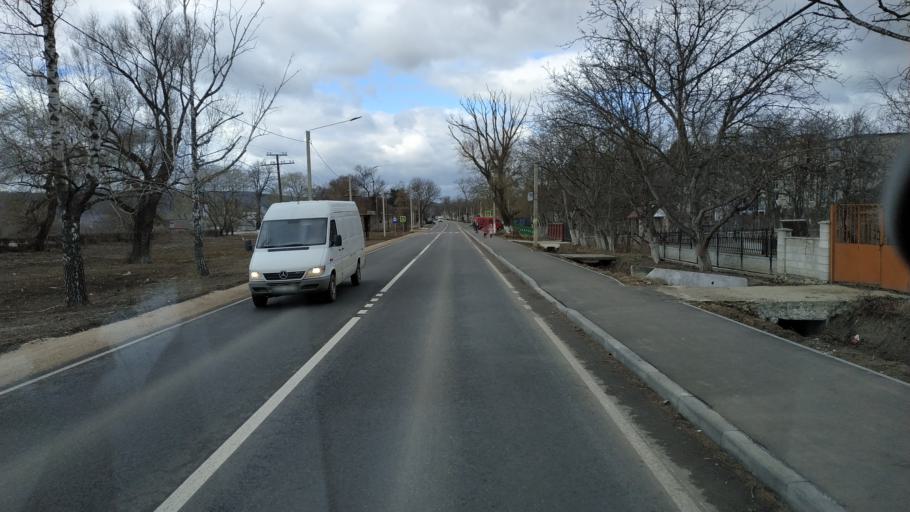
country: MD
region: Stinga Nistrului
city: Bucovat
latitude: 47.1872
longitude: 28.4601
